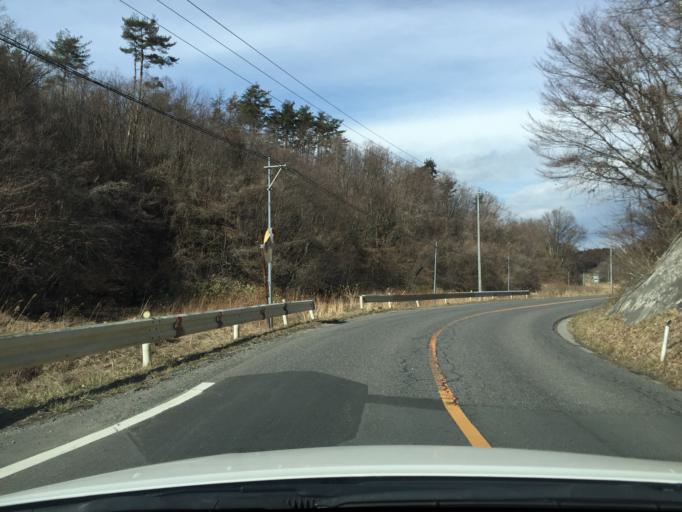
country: JP
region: Fukushima
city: Funehikimachi-funehiki
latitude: 37.4044
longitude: 140.5478
